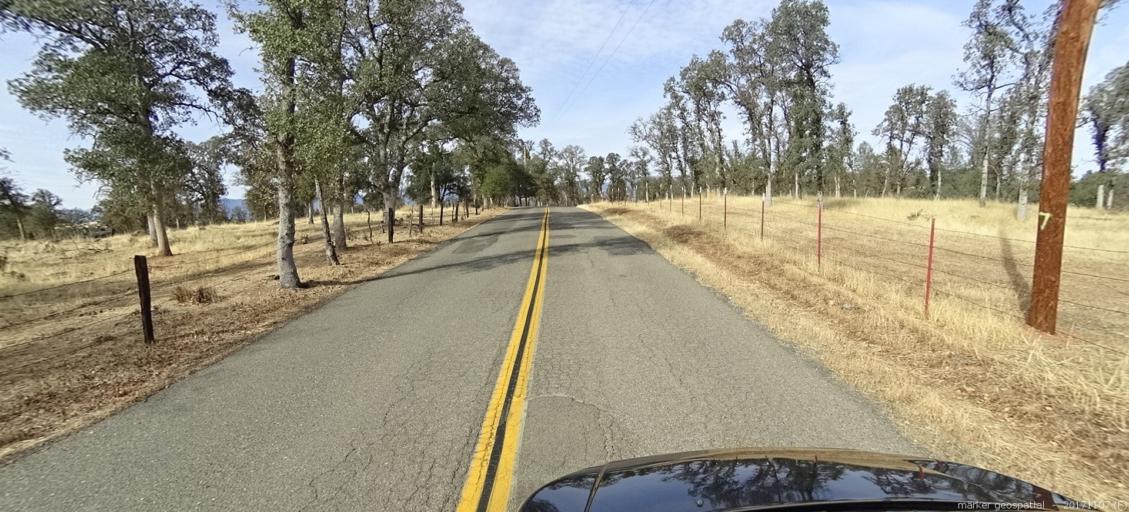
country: US
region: California
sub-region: Shasta County
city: Shasta
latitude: 40.4138
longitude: -122.5221
